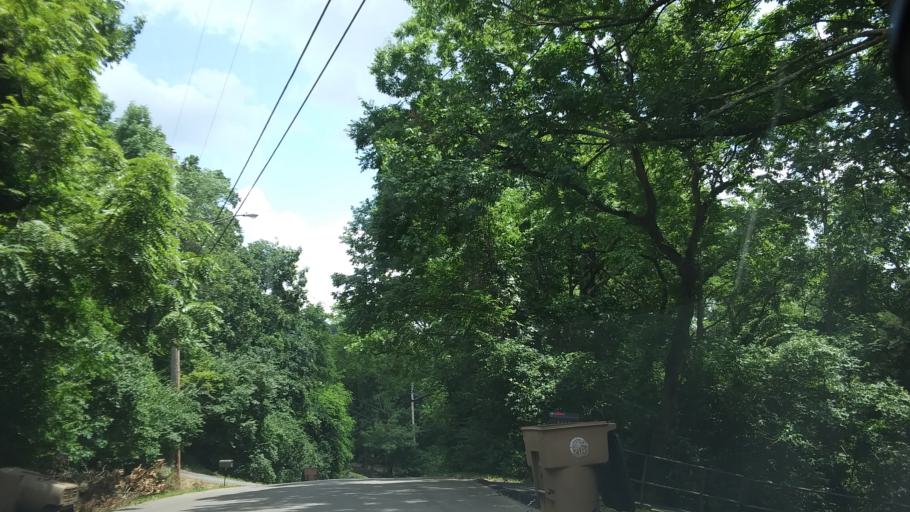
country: US
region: Tennessee
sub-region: Davidson County
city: Belle Meade
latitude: 36.1397
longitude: -86.8743
